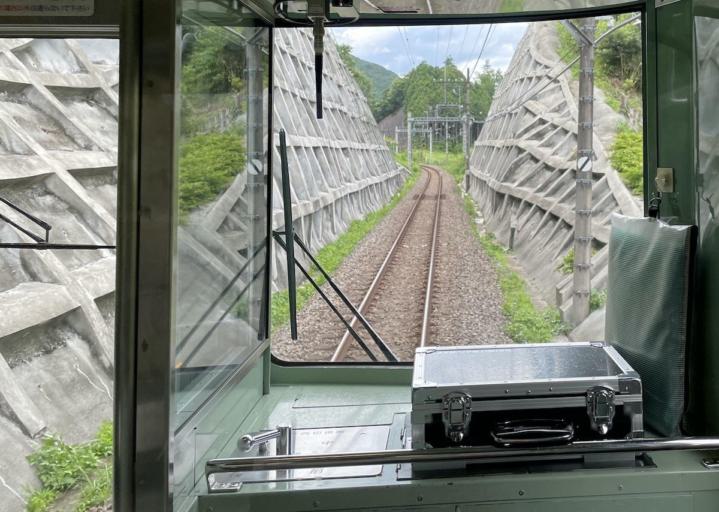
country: JP
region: Saitama
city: Morohongo
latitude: 35.8963
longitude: 139.2547
